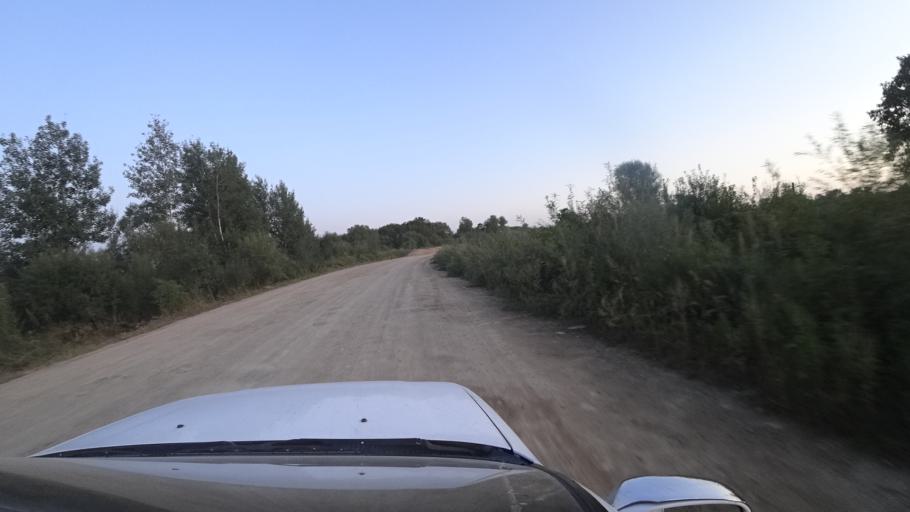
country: RU
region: Primorskiy
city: Dal'nerechensk
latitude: 45.9418
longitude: 133.7611
